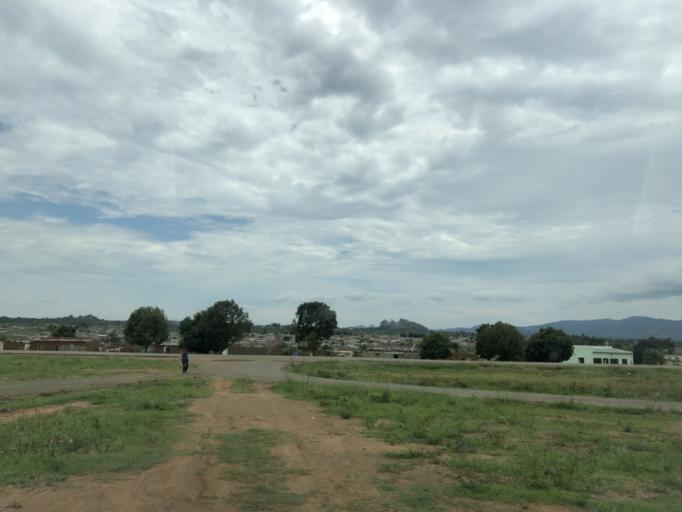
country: AO
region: Cuanza Sul
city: Quibala
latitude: -10.7278
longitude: 14.9715
